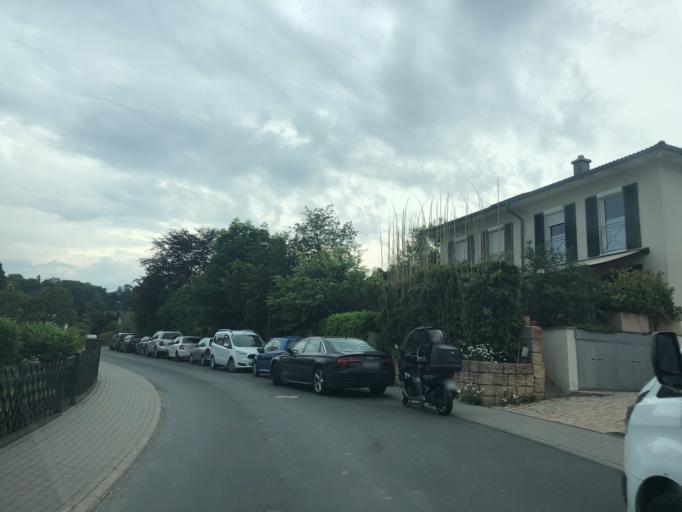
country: DE
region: Hesse
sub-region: Regierungsbezirk Darmstadt
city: Konigstein im Taunus
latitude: 50.1756
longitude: 8.4676
